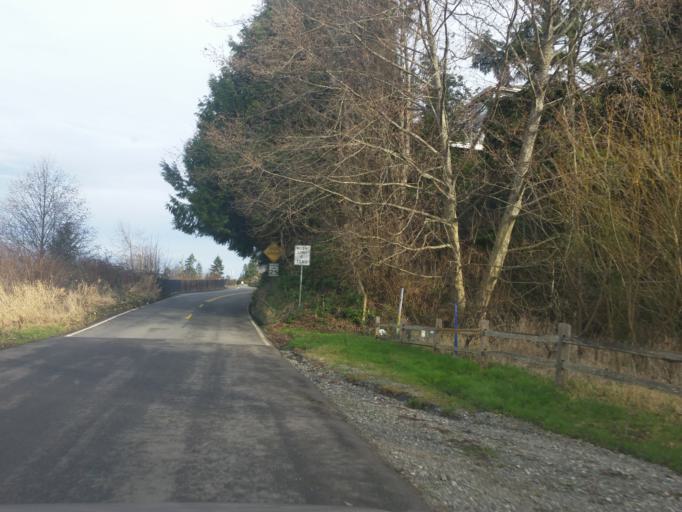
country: US
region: Washington
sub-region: Snohomish County
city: Mukilteo
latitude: 47.9503
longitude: -122.2930
